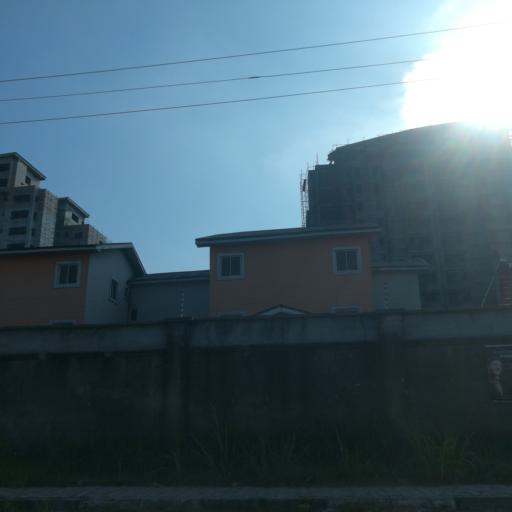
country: NG
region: Rivers
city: Port Harcourt
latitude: 4.8011
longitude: 7.0269
